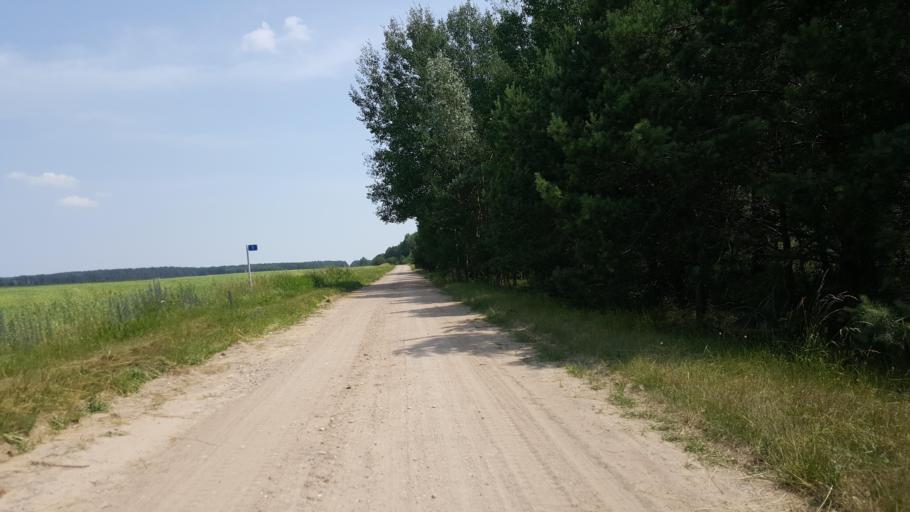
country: BY
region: Brest
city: Kamyanyets
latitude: 52.3524
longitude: 23.7570
